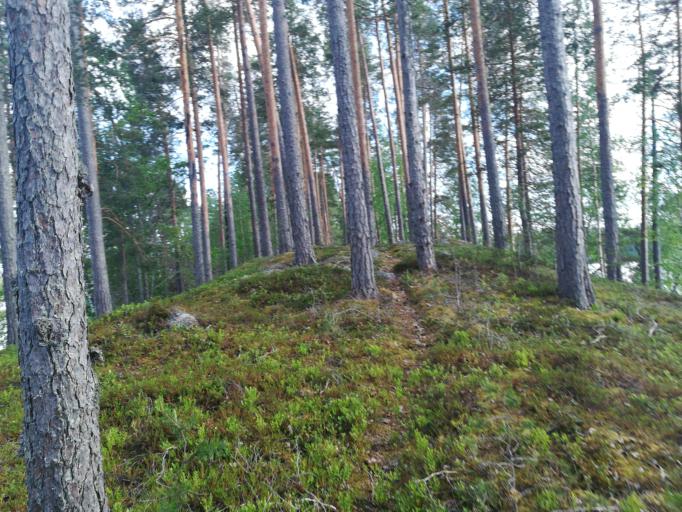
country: FI
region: Southern Savonia
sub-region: Savonlinna
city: Savonlinna
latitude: 61.6418
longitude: 28.7129
